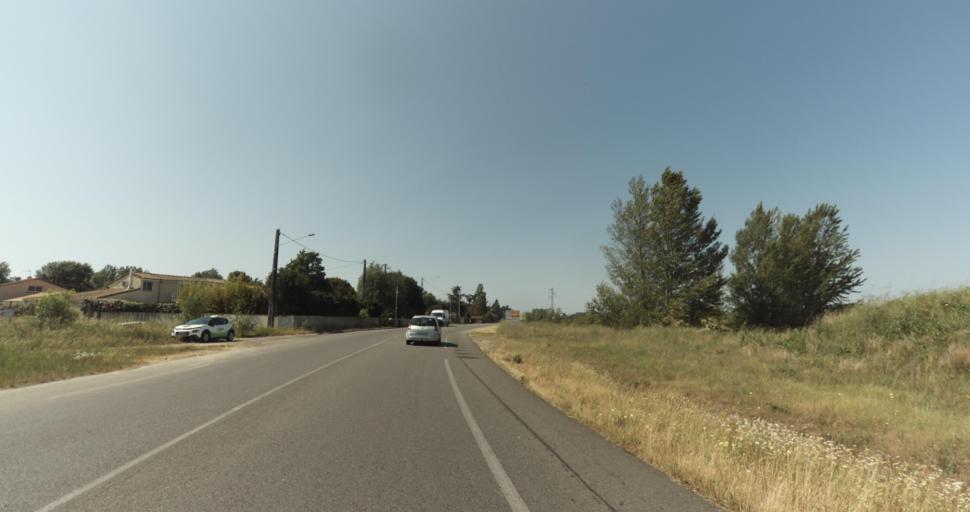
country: FR
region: Midi-Pyrenees
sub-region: Departement de la Haute-Garonne
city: La Salvetat-Saint-Gilles
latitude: 43.5861
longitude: 1.2802
